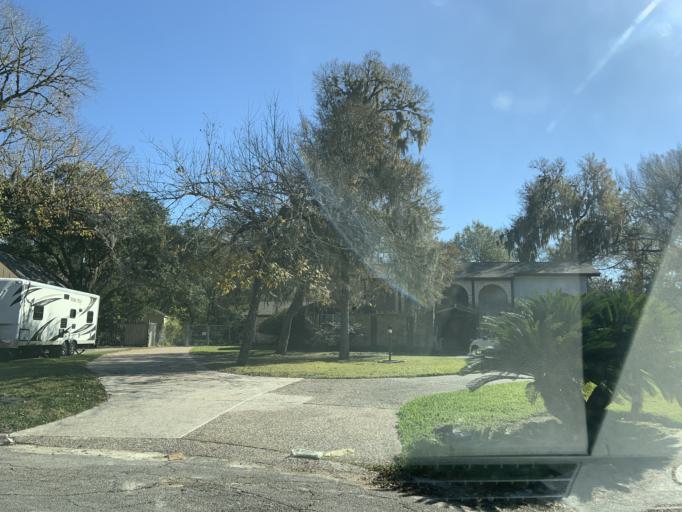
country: US
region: Texas
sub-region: Fort Bend County
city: Missouri City
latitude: 29.6765
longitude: -95.5144
